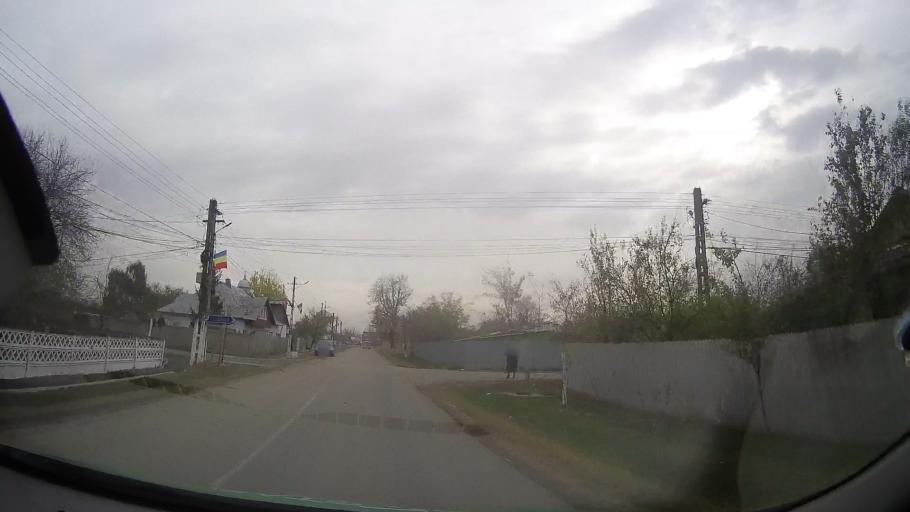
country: RO
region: Prahova
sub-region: Comuna Dumbrava
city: Dumbrava
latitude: 44.8754
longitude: 26.1864
